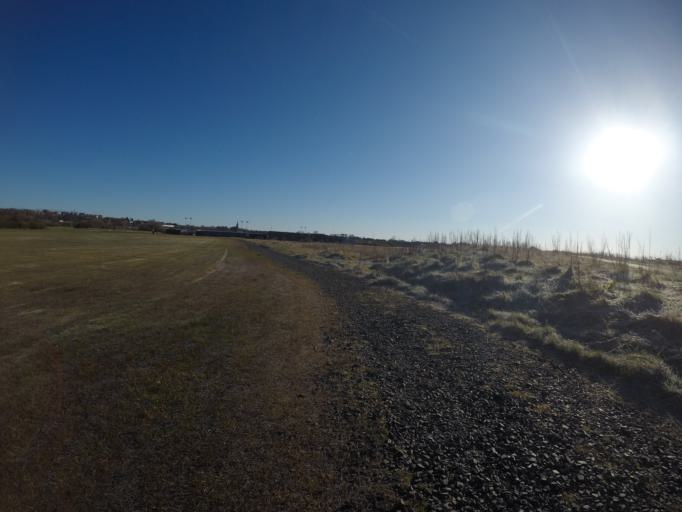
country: GB
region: Scotland
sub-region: North Ayrshire
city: Stevenston
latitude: 55.6345
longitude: -4.7635
